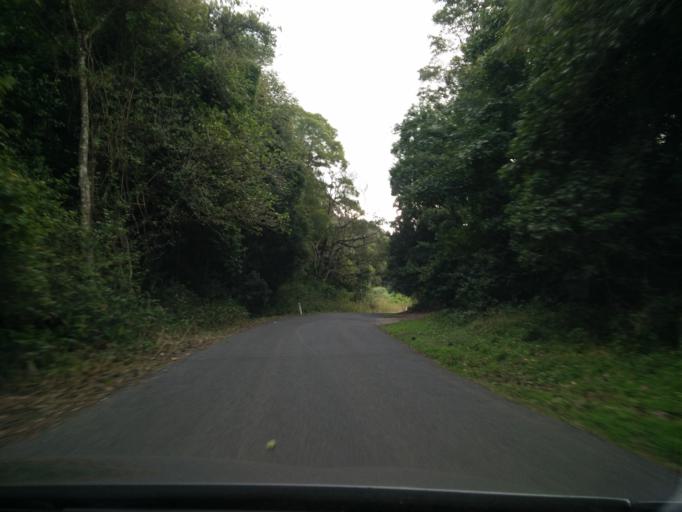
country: AU
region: New South Wales
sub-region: Kiama
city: Jamberoo
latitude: -34.6964
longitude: 150.7946
